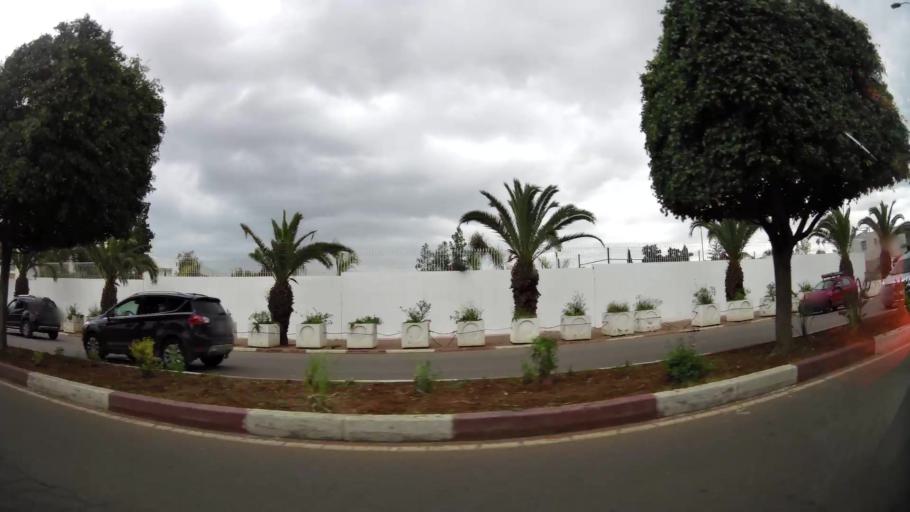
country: MA
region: Grand Casablanca
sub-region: Casablanca
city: Casablanca
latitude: 33.5363
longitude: -7.6303
